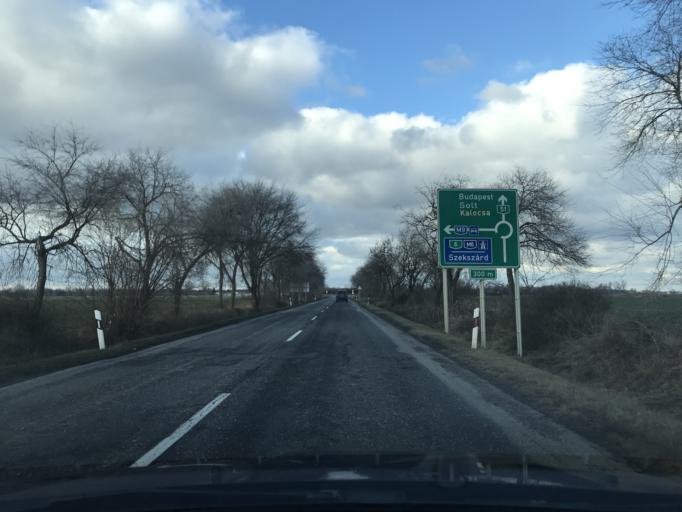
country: HU
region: Bacs-Kiskun
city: Dusnok
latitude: 46.3515
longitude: 18.9685
